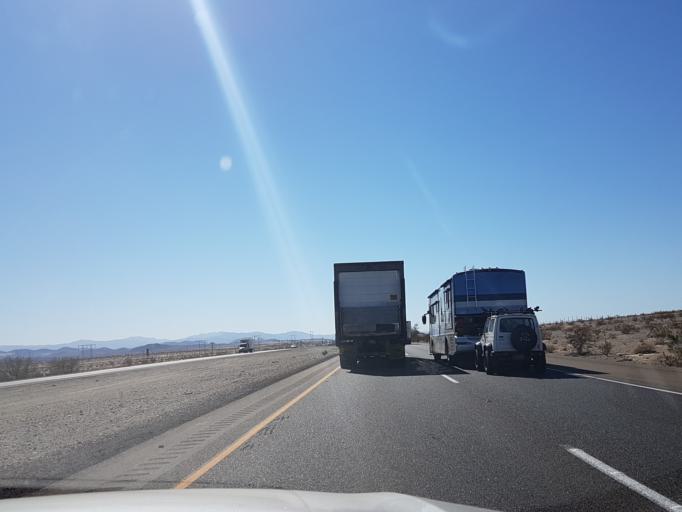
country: US
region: California
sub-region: San Bernardino County
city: Fort Irwin
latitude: 35.0418
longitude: -116.4572
